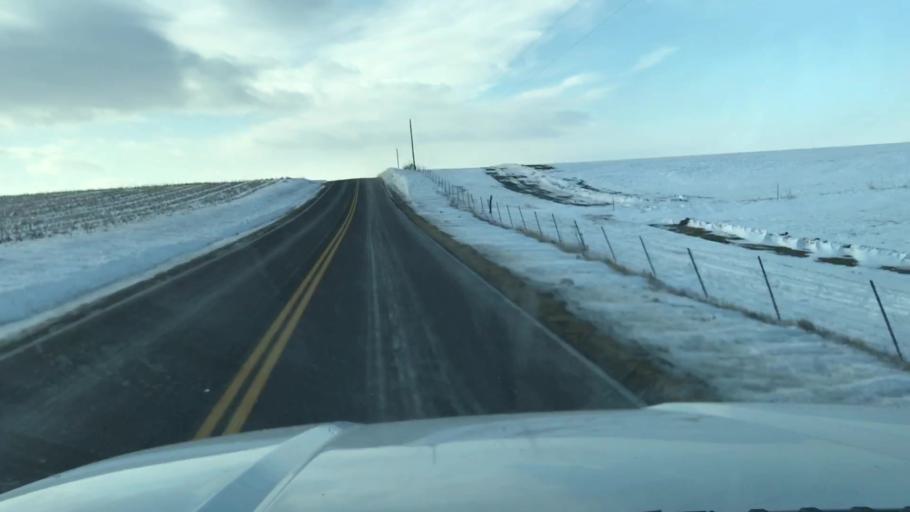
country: US
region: Missouri
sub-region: Nodaway County
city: Maryville
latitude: 40.2011
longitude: -94.9083
